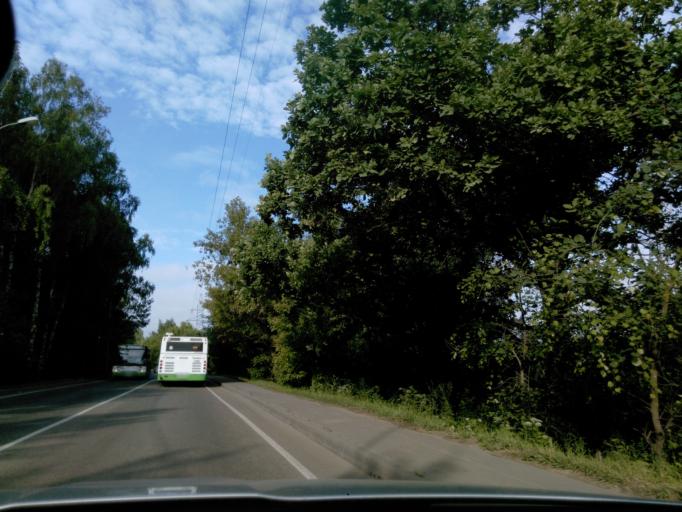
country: RU
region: Moskovskaya
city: Levoberezhnaya
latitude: 55.8793
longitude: 37.4760
